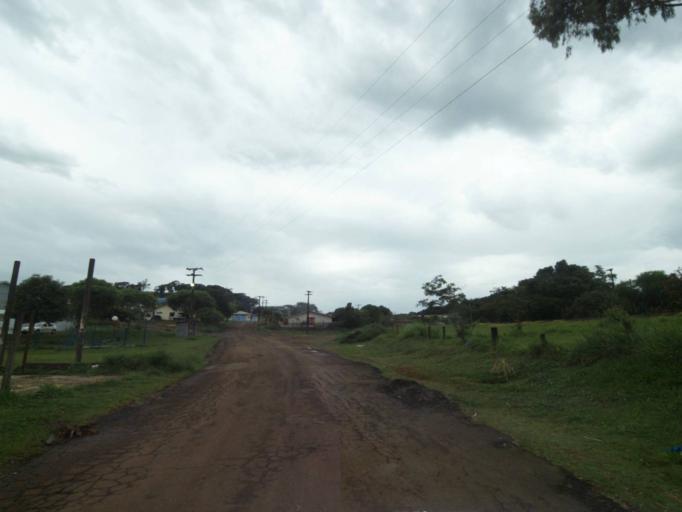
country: BR
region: Parana
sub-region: Guaraniacu
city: Guaraniacu
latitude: -25.1117
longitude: -52.8527
